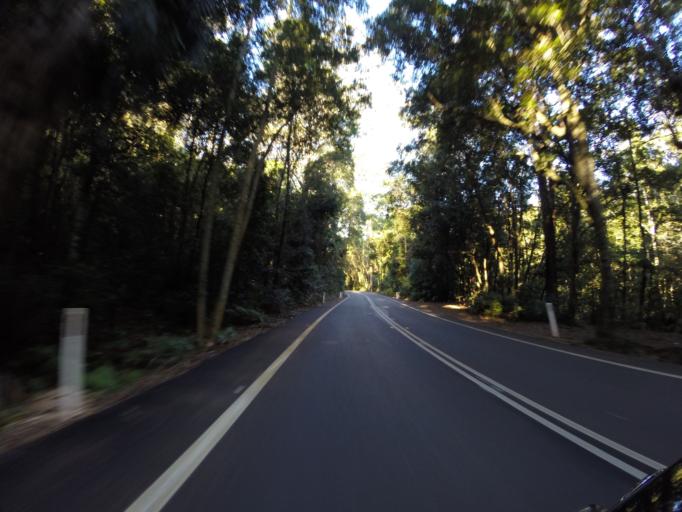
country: AU
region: New South Wales
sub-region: Wollongong
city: Helensburgh
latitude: -34.1703
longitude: 151.0189
